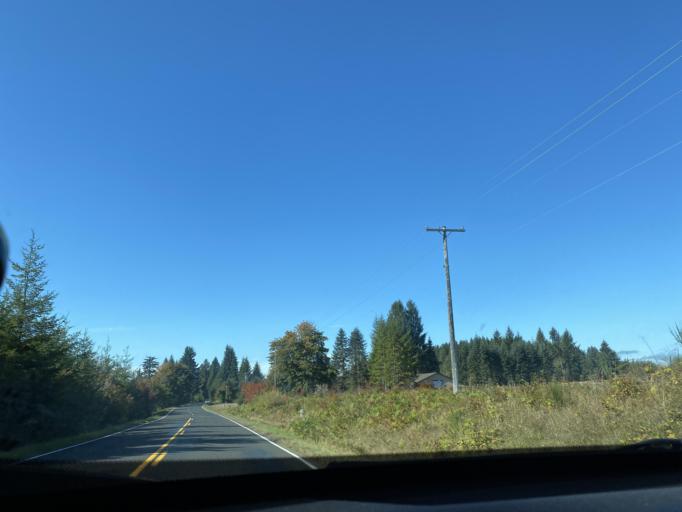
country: US
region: Washington
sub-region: Clallam County
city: Forks
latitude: 47.9483
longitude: -124.5121
